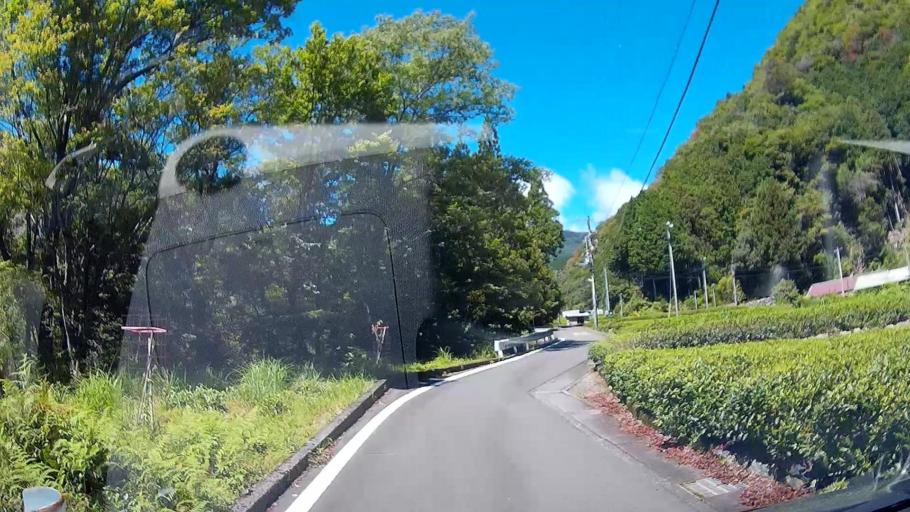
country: JP
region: Shizuoka
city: Fujinomiya
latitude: 35.2833
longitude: 138.3274
